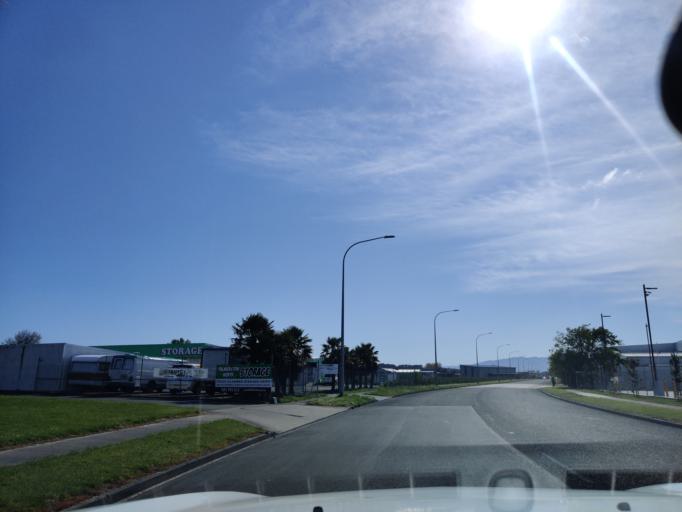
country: NZ
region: Manawatu-Wanganui
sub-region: Palmerston North City
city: Palmerston North
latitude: -40.3338
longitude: 175.6455
